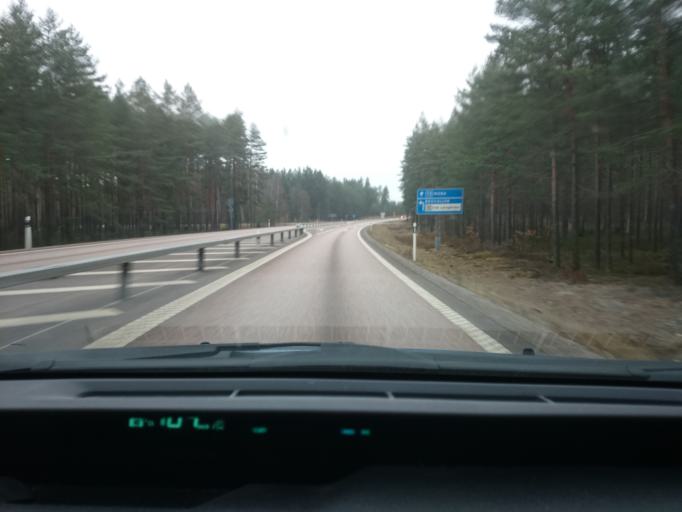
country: SE
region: Dalarna
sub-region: Avesta Kommun
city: Avesta
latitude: 60.0825
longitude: 16.3178
